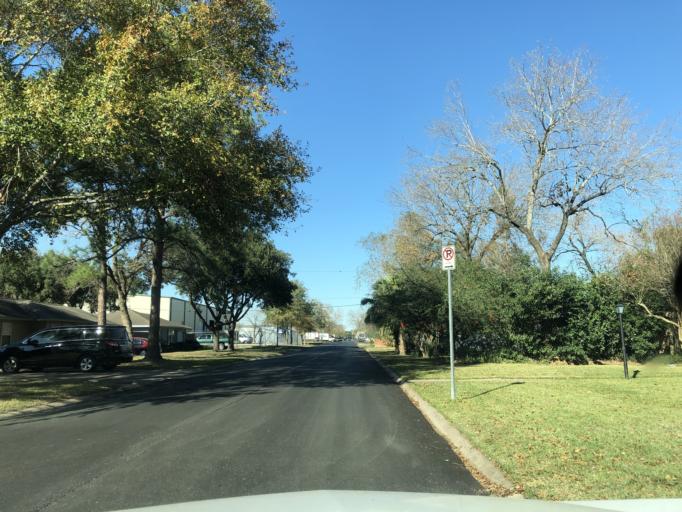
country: US
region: Texas
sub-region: Harris County
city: Bellaire
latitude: 29.6883
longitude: -95.4969
